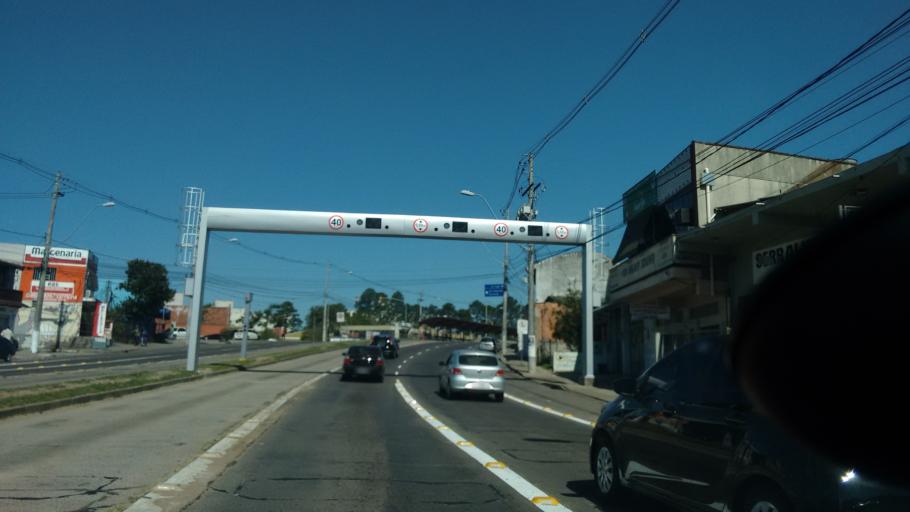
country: BR
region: Rio Grande do Sul
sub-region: Cachoeirinha
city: Cachoeirinha
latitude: -30.0125
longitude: -51.1249
